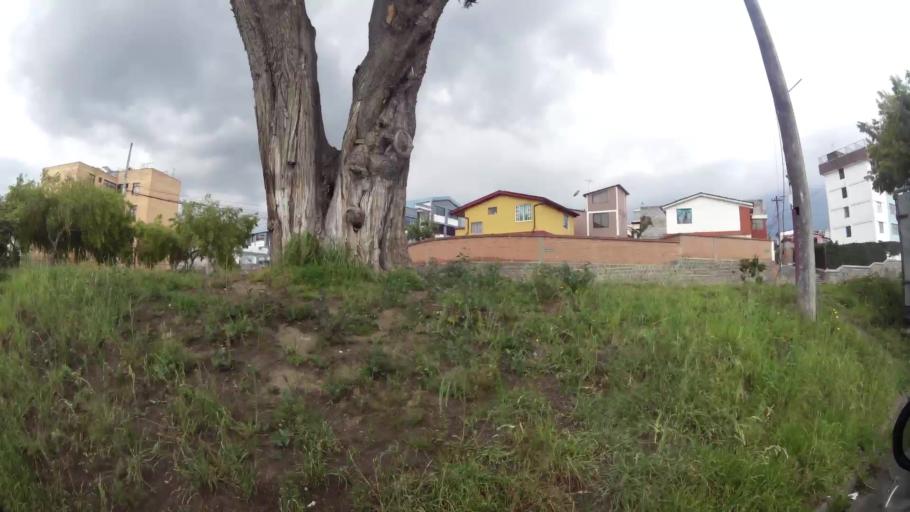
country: EC
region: Pichincha
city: Quito
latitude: -0.0842
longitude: -78.4706
